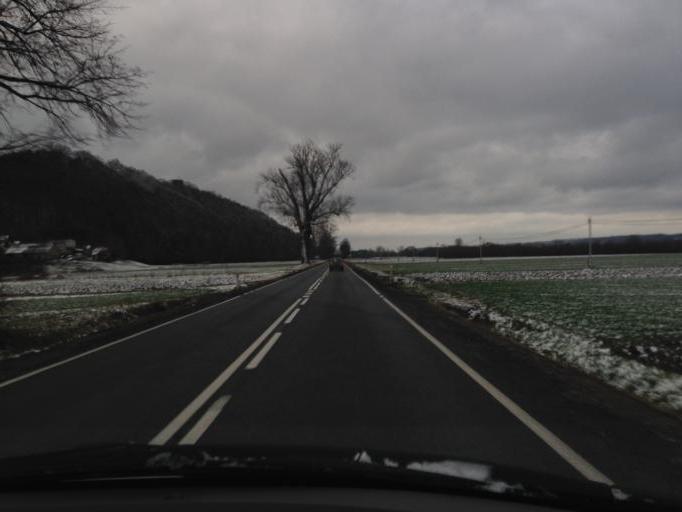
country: PL
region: Lesser Poland Voivodeship
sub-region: Powiat tarnowski
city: Zakliczyn
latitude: 49.8685
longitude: 20.7593
